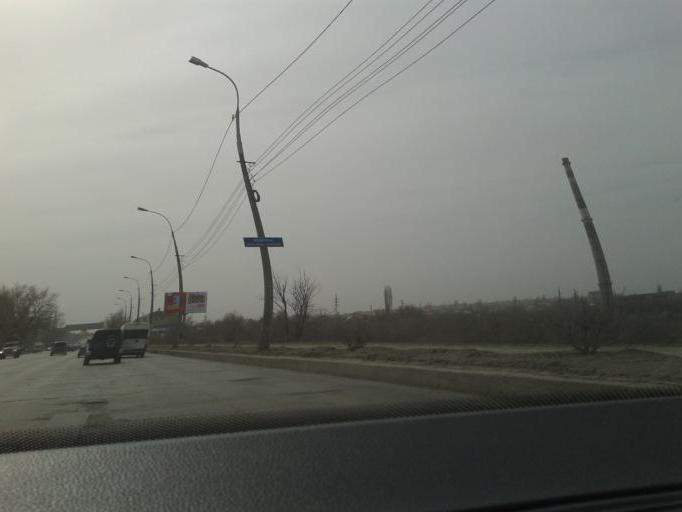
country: RU
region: Volgograd
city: Volgograd
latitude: 48.7079
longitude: 44.4879
